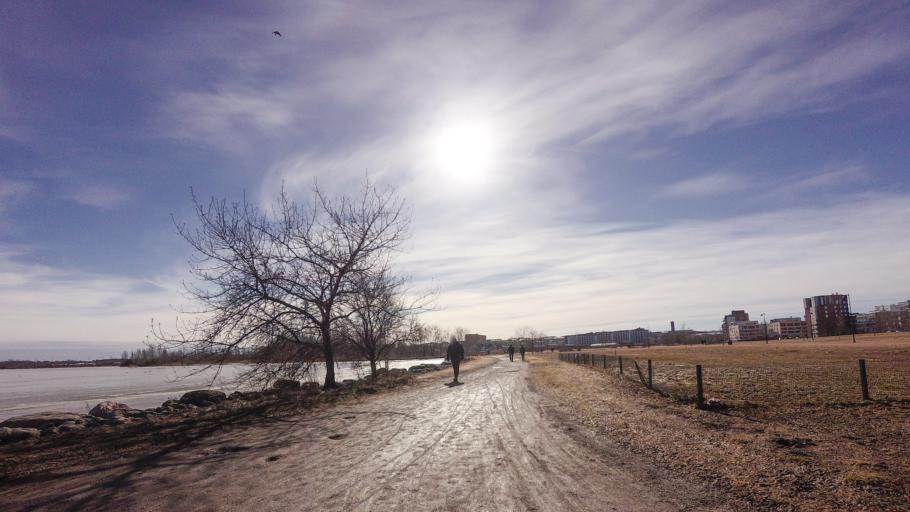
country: FI
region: Uusimaa
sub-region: Helsinki
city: Helsinki
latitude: 60.2030
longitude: 24.9794
